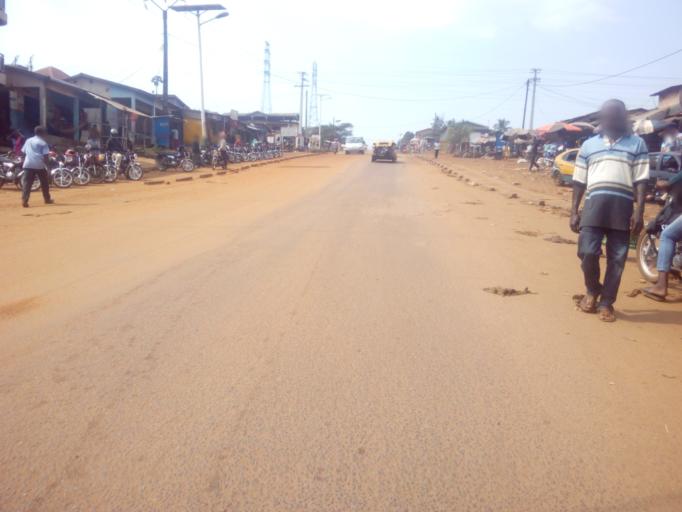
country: GN
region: Conakry
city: Conakry
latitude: 9.6343
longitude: -13.5722
